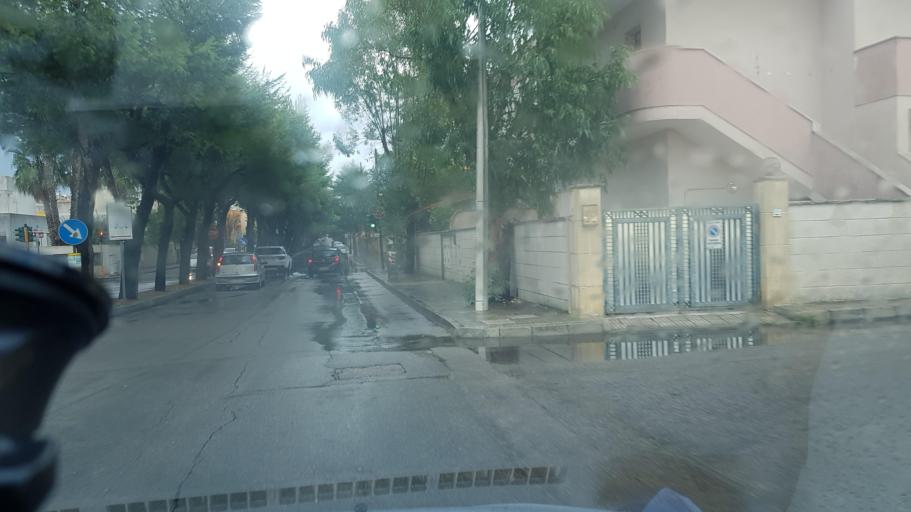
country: IT
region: Apulia
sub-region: Provincia di Lecce
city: Giorgilorio
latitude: 40.3846
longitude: 18.1444
